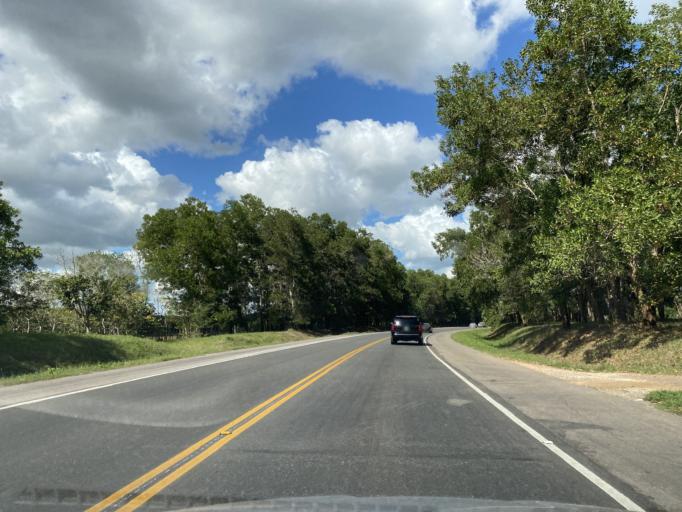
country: DO
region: Monte Plata
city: Monte Plata
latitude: 18.7491
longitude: -69.7660
